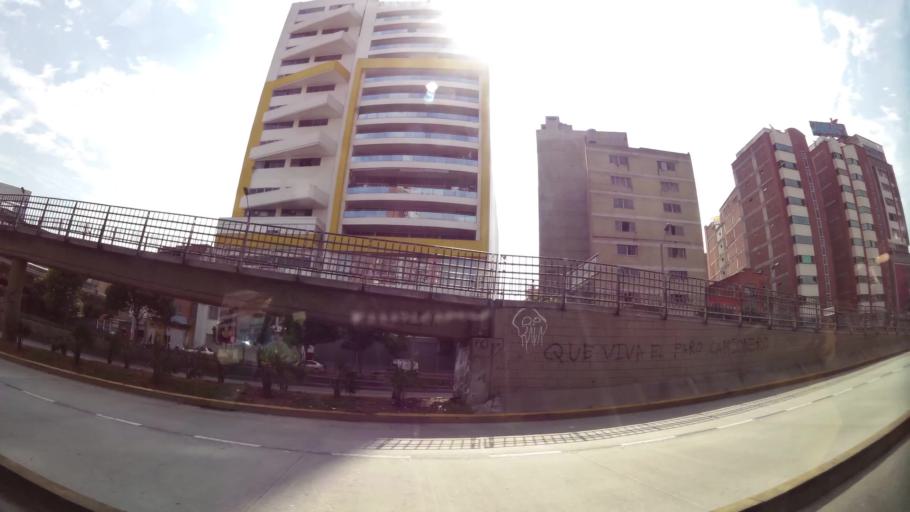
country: CO
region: Antioquia
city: Medellin
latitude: 6.2521
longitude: -75.5747
